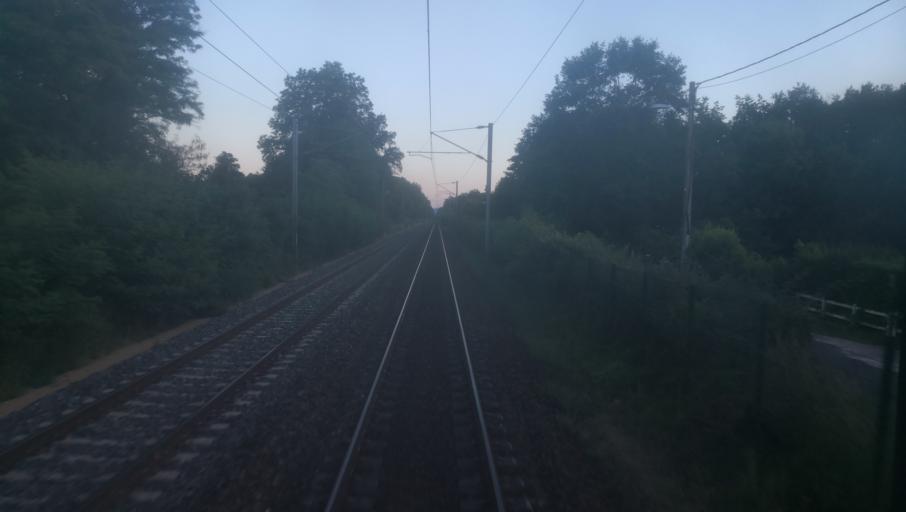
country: FR
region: Bourgogne
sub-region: Departement de la Nievre
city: Cosne-Cours-sur-Loire
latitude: 47.3663
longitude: 2.8957
